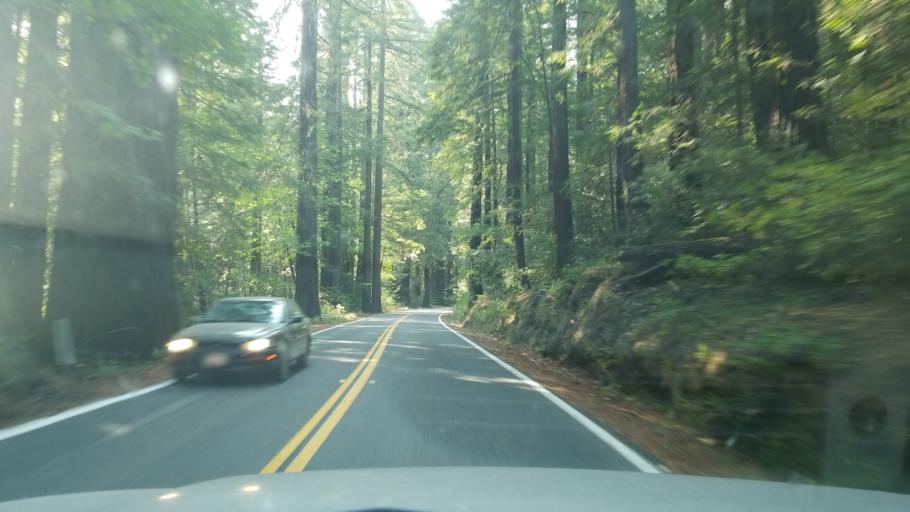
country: US
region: California
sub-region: Humboldt County
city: Redway
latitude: 40.2589
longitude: -123.8392
